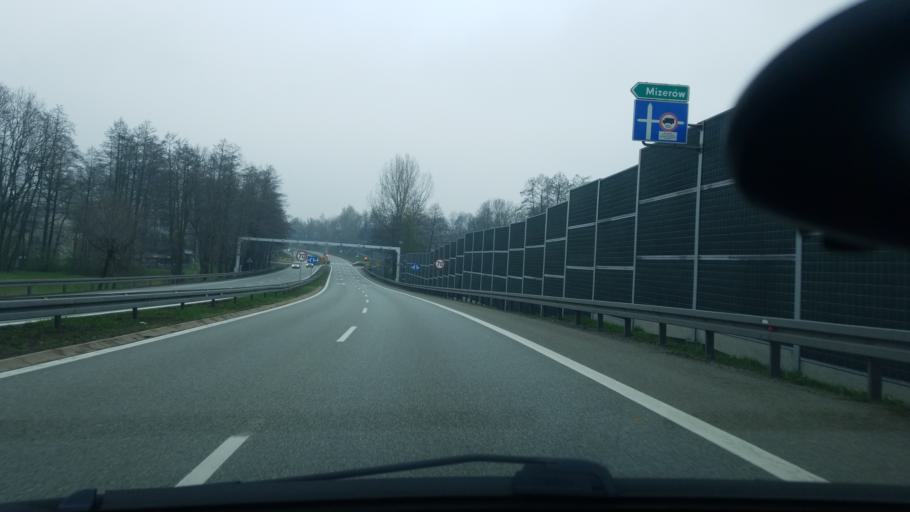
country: PL
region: Silesian Voivodeship
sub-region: Powiat pszczynski
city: Pawlowice
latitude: 49.9691
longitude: 18.7179
